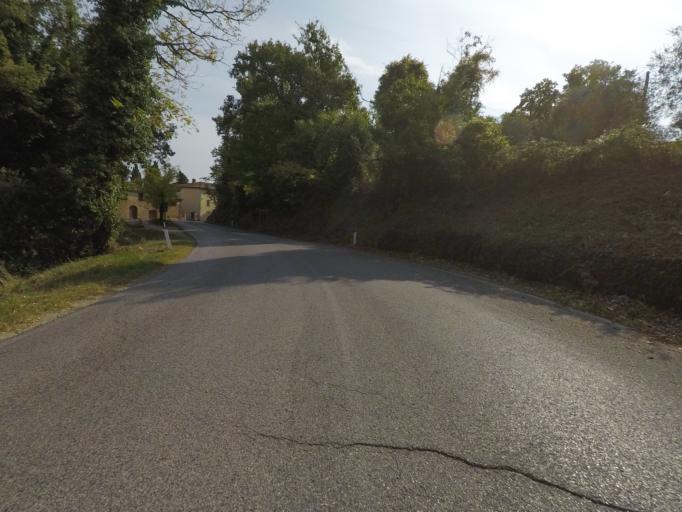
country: IT
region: Tuscany
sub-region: Provincia di Siena
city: Radda in Chianti
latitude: 43.4147
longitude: 11.3493
